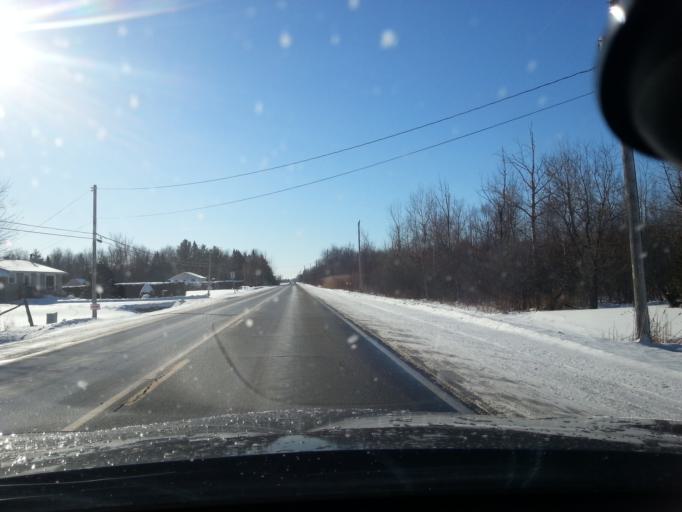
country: CA
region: Ontario
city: Ottawa
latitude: 45.3185
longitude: -75.4770
